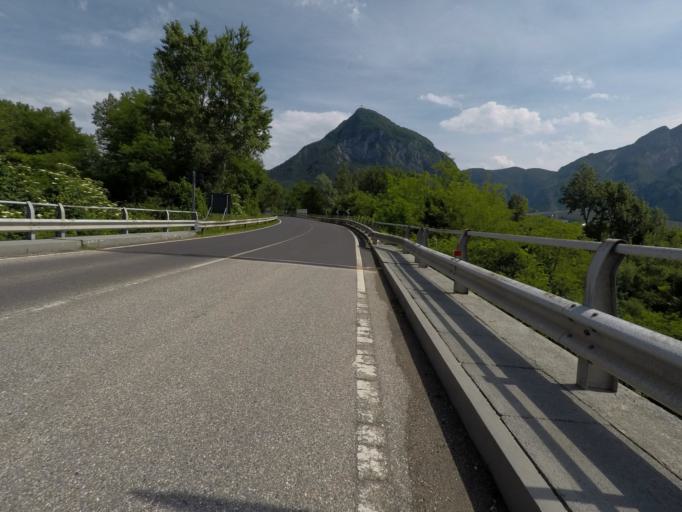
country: IT
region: Friuli Venezia Giulia
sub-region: Provincia di Udine
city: Tolmezzo
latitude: 46.3917
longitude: 13.0141
